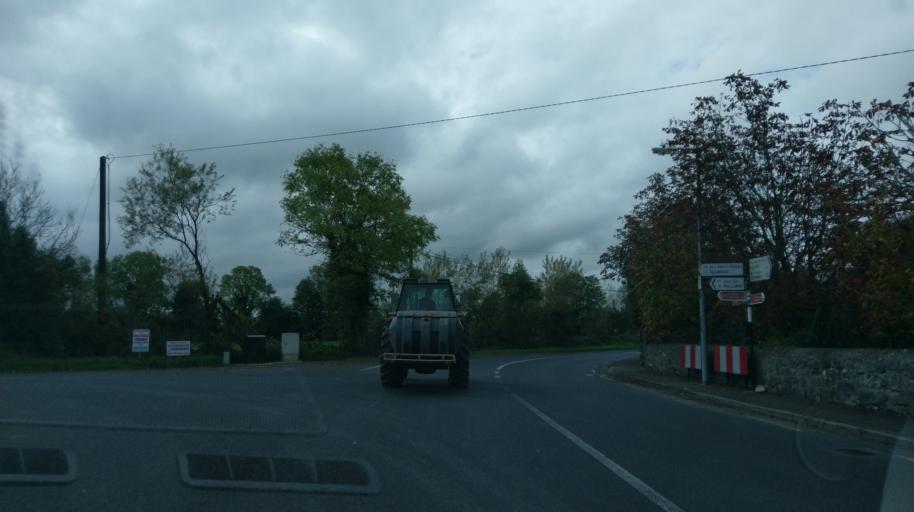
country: IE
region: Connaught
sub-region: County Galway
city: Ballinasloe
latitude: 53.3950
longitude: -8.3394
